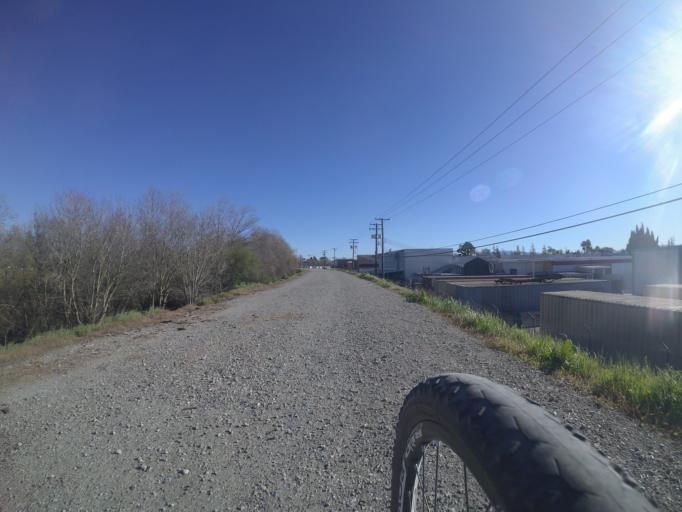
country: US
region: California
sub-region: Santa Clara County
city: Santa Clara
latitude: 37.3891
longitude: -121.9391
